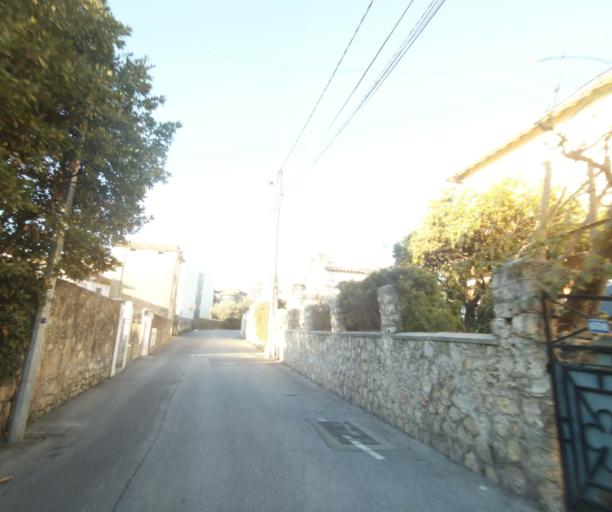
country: FR
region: Provence-Alpes-Cote d'Azur
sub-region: Departement des Alpes-Maritimes
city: Antibes
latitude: 43.5766
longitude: 7.0985
